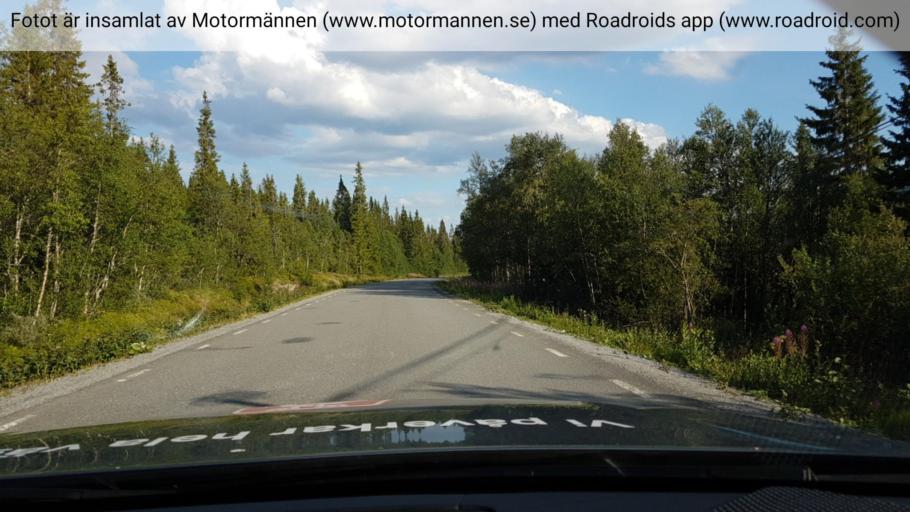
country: SE
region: Jaemtland
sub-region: Are Kommun
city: Are
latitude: 63.4178
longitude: 13.0219
